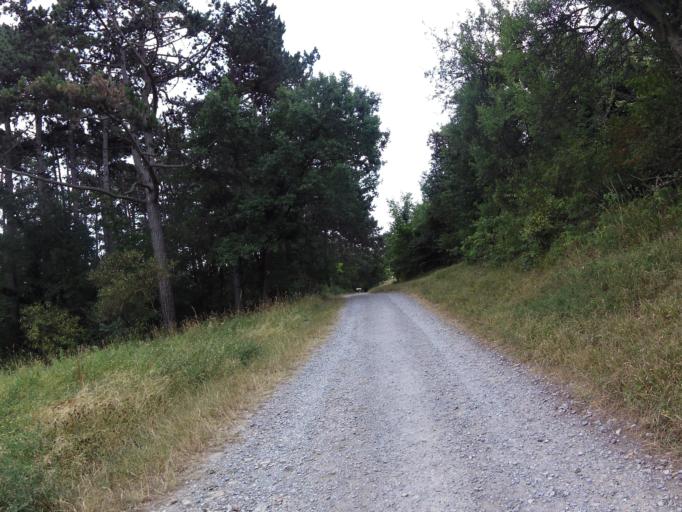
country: DE
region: Bavaria
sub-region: Regierungsbezirk Unterfranken
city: Gerbrunn
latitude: 49.7734
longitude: 9.9898
